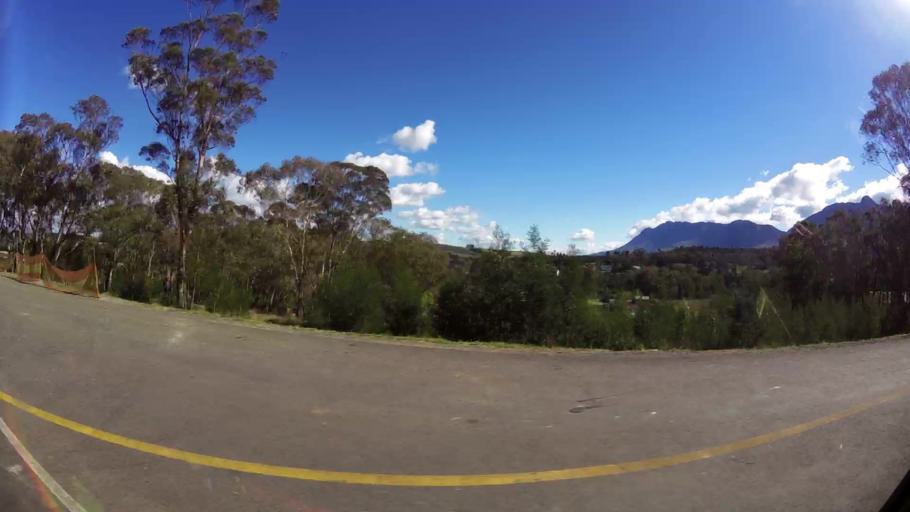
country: ZA
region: Western Cape
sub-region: Overberg District Municipality
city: Swellendam
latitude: -34.0388
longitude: 20.4330
